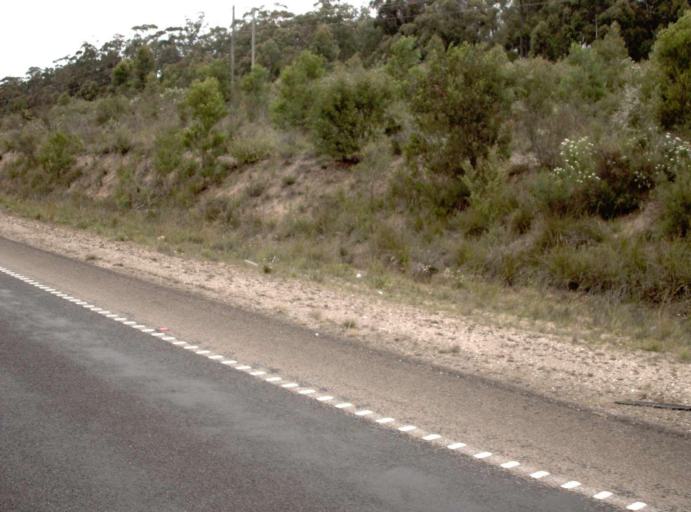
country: AU
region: Victoria
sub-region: East Gippsland
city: Lakes Entrance
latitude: -37.6976
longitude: 148.0487
